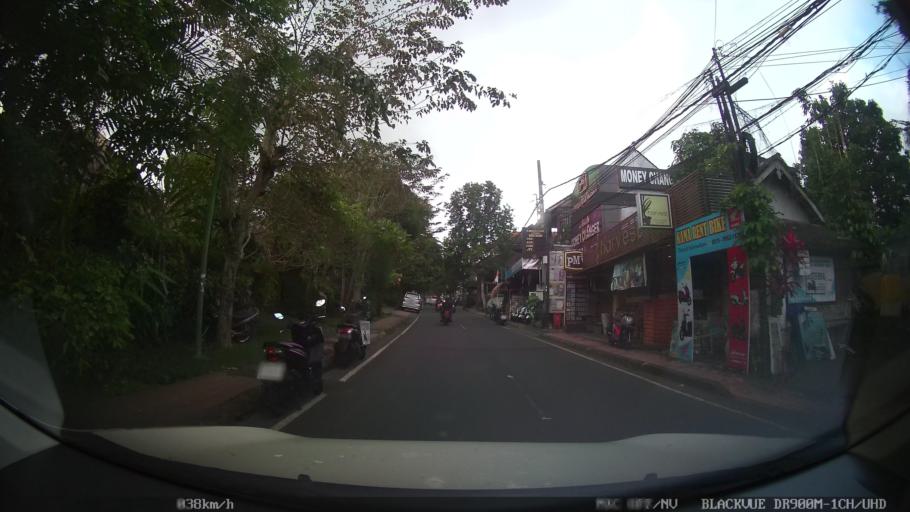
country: ID
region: Bali
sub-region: Kabupaten Gianyar
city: Ubud
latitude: -8.4962
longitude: 115.2535
